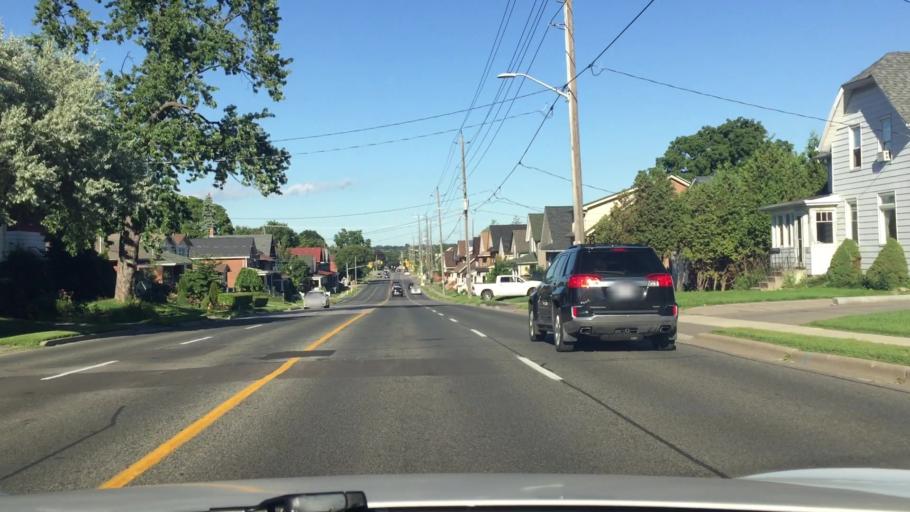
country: CA
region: Ontario
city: Oshawa
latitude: 43.9050
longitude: -78.8630
